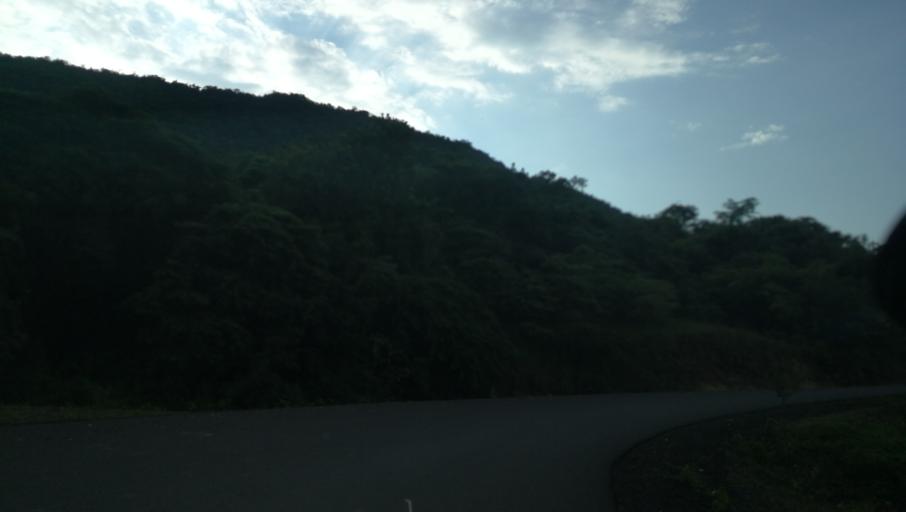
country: ET
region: Southern Nations, Nationalities, and People's Region
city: Areka
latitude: 6.8493
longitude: 37.2724
